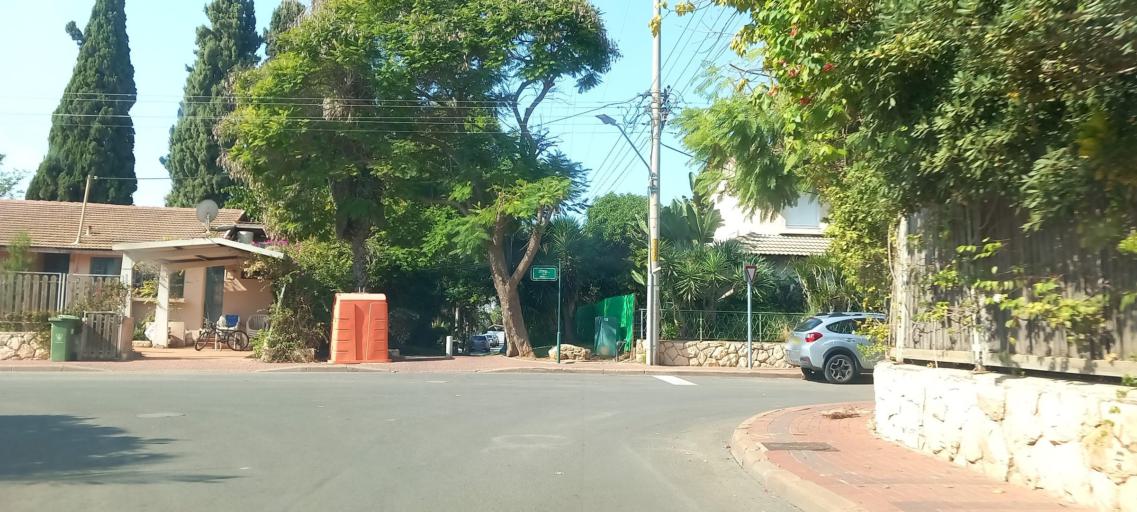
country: IL
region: Tel Aviv
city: Or Yehuda
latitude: 32.0452
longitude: 34.8328
